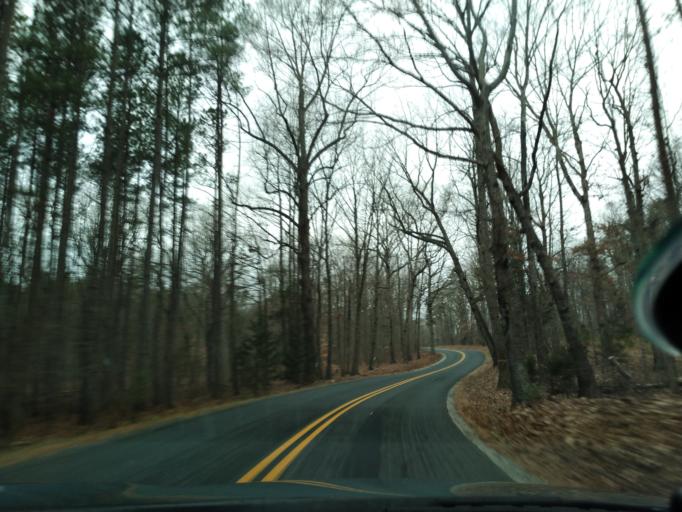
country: US
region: Virginia
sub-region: Buckingham County
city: Buckingham
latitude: 37.4355
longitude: -78.6325
